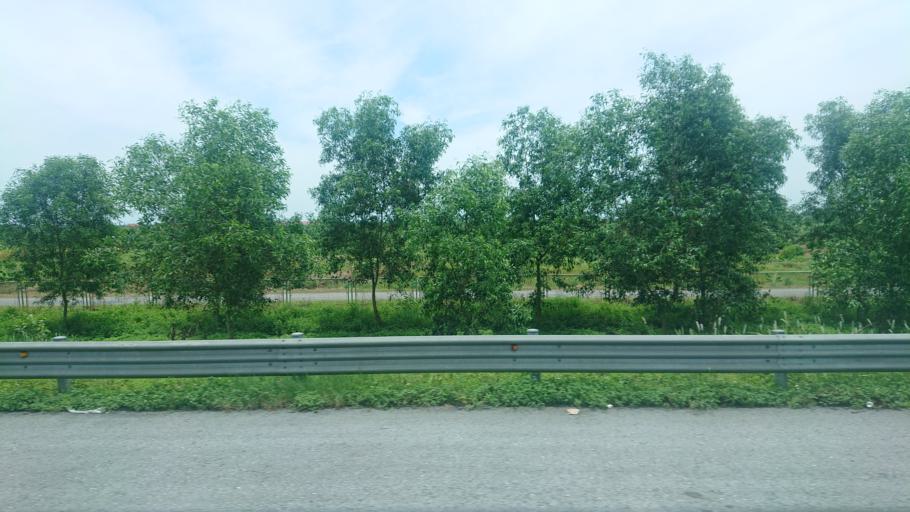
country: VN
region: Hai Phong
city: An Lao
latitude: 20.8178
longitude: 106.4856
